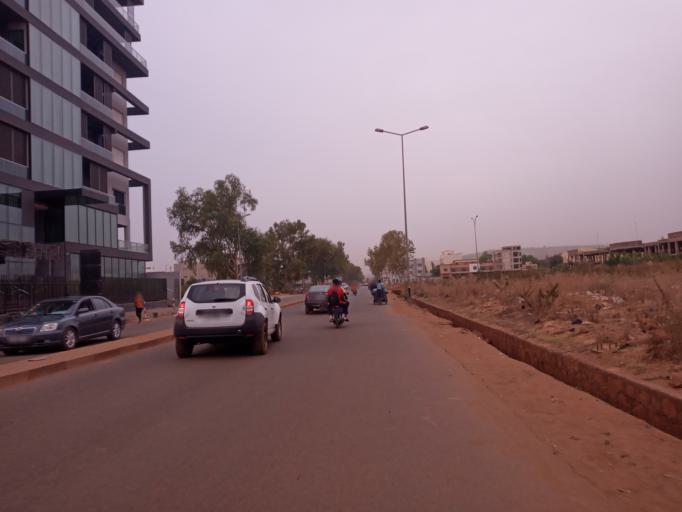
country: ML
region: Bamako
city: Bamako
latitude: 12.6317
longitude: -8.0290
